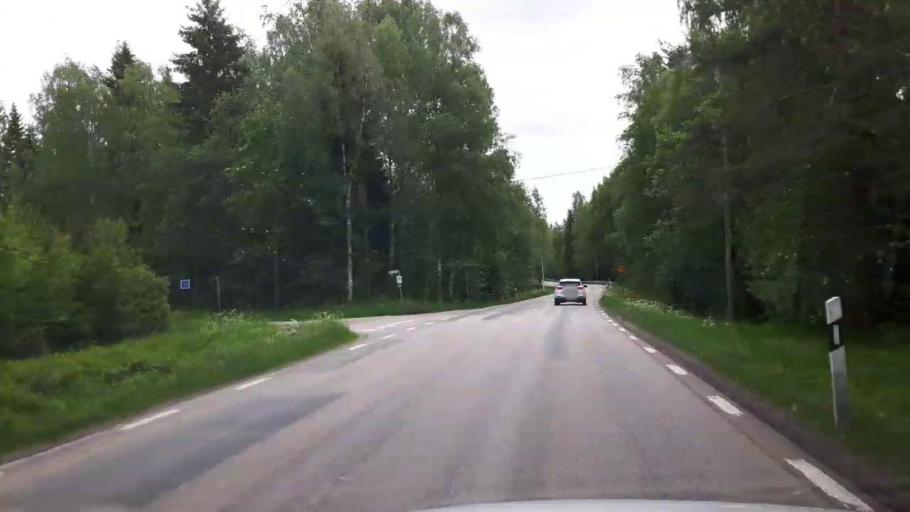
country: SE
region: Vaestmanland
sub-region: Norbergs Kommun
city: Norberg
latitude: 60.1118
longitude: 15.9190
